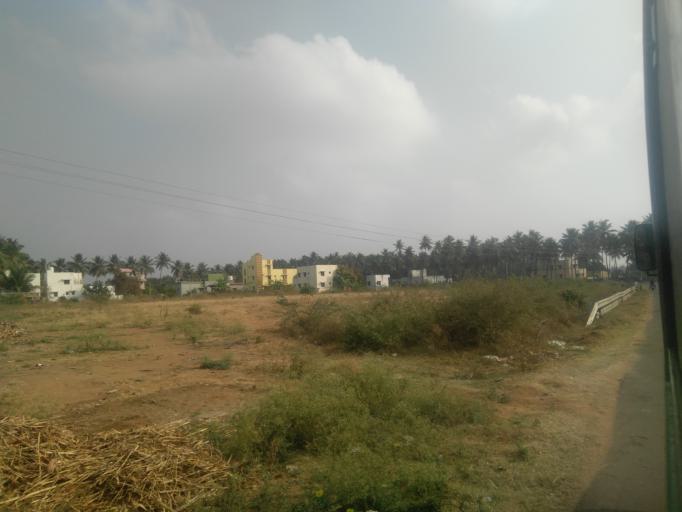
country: IN
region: Tamil Nadu
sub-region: Coimbatore
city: Coimbatore
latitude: 11.0669
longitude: 76.9195
